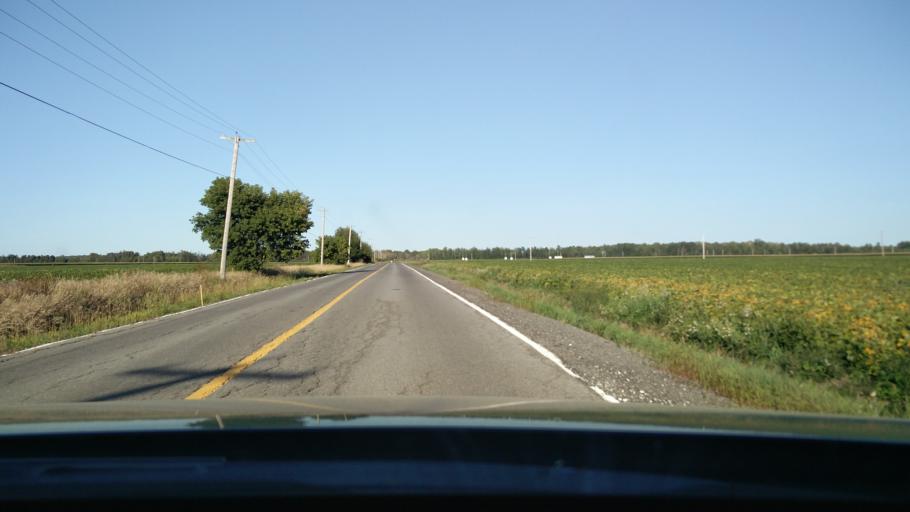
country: CA
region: Ontario
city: Bells Corners
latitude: 45.2123
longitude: -75.7851
